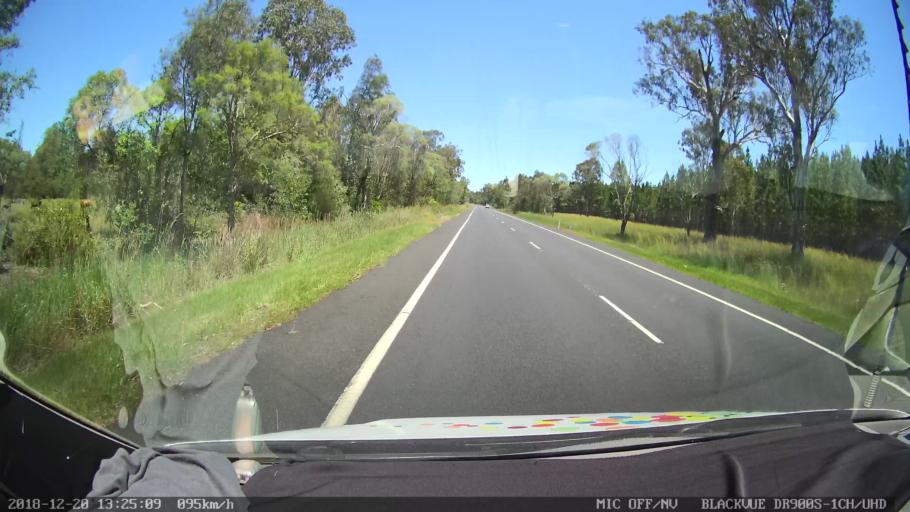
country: AU
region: New South Wales
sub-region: Richmond Valley
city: Casino
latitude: -29.1271
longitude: 152.9975
